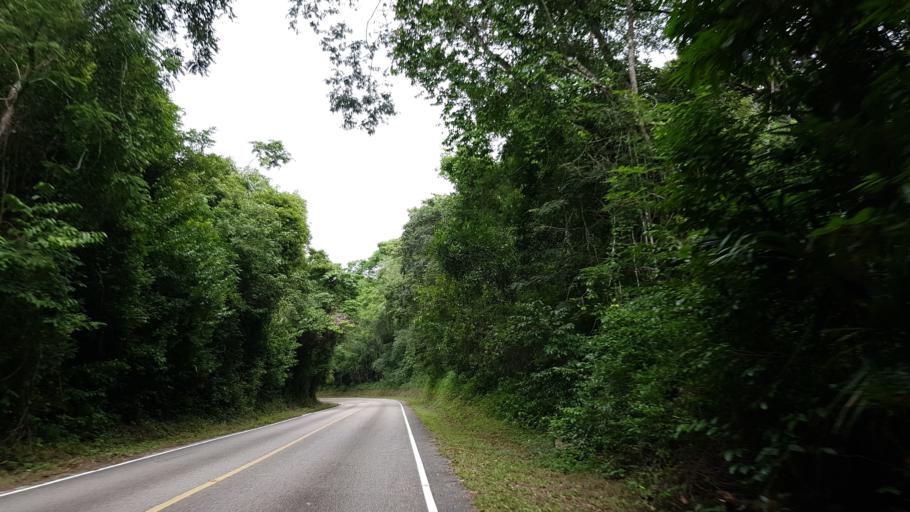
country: GT
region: Peten
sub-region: Municipio de San Jose
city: San Jose
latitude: 17.2100
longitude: -89.6174
